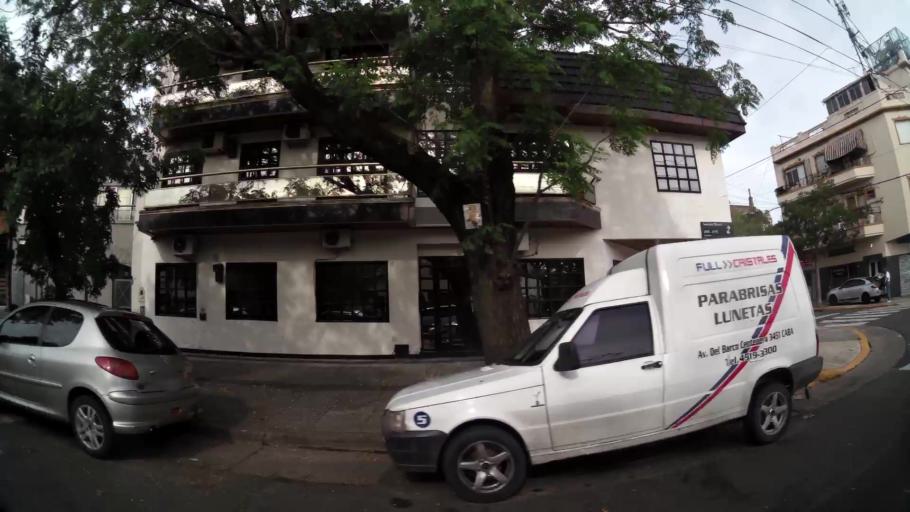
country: AR
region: Buenos Aires F.D.
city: Villa Lugano
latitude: -34.6426
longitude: -58.4309
